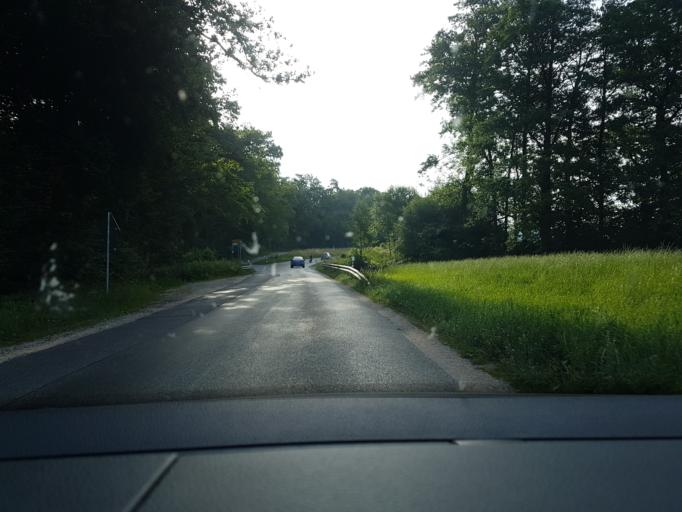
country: DE
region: Bavaria
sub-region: Upper Bavaria
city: Ainring
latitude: 47.8609
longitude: 12.9207
